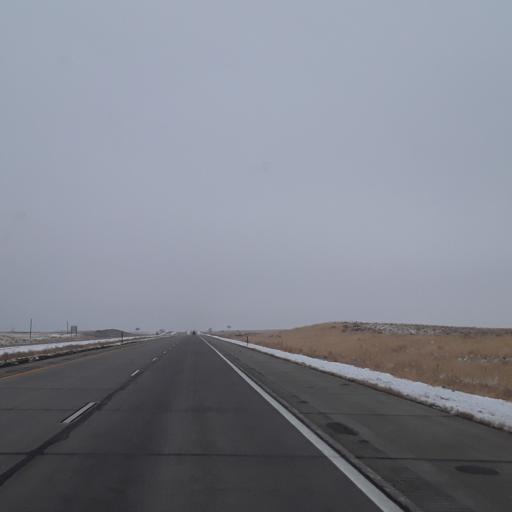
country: US
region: Colorado
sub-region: Logan County
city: Sterling
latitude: 40.5121
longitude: -103.2495
